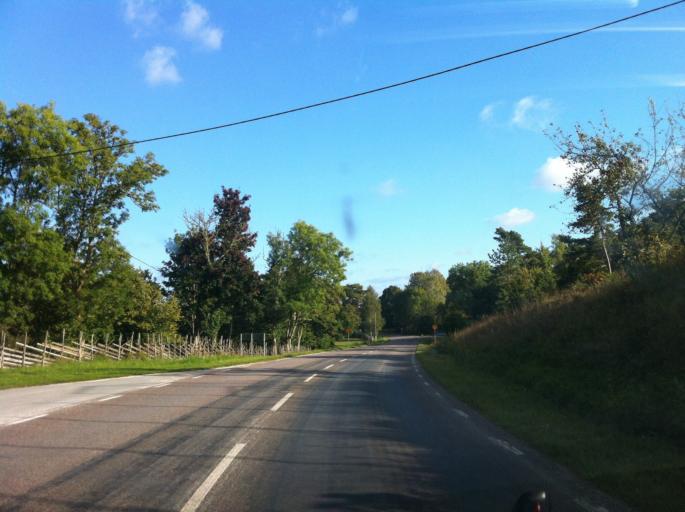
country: SE
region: Gotland
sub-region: Gotland
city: Slite
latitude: 57.4215
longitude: 18.8589
